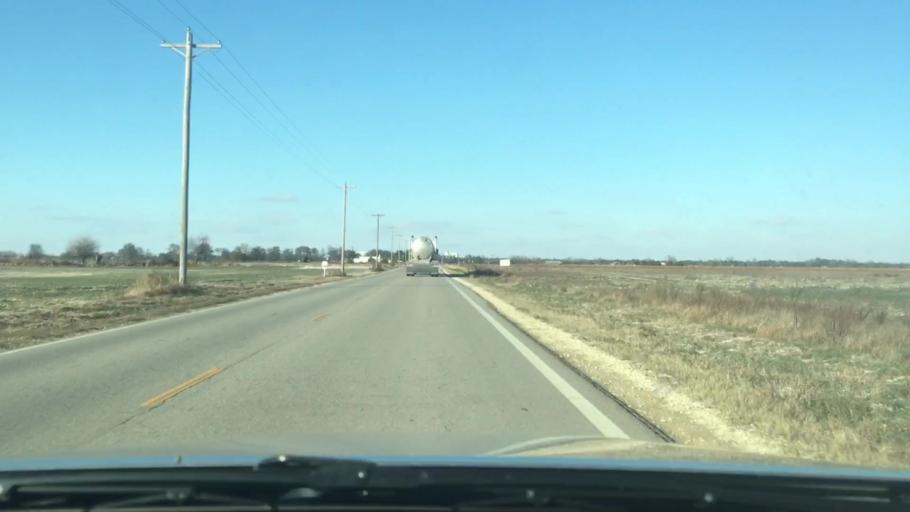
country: US
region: Kansas
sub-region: Rice County
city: Sterling
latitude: 38.1792
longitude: -98.2069
